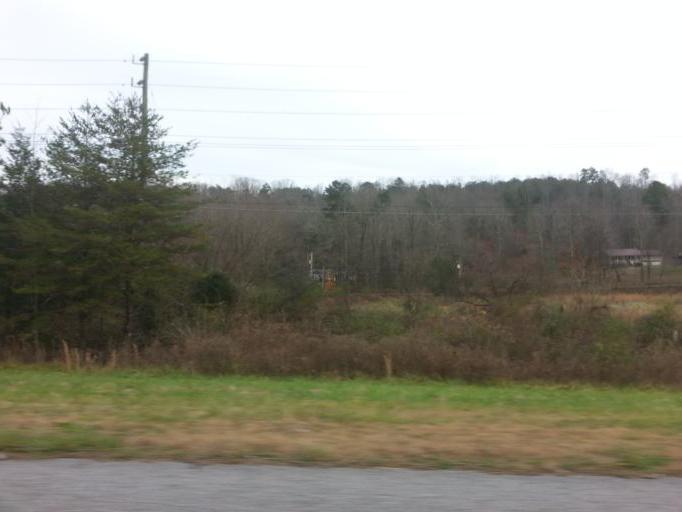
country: US
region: Tennessee
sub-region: Hamilton County
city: Sale Creek
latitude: 35.3611
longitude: -85.1200
